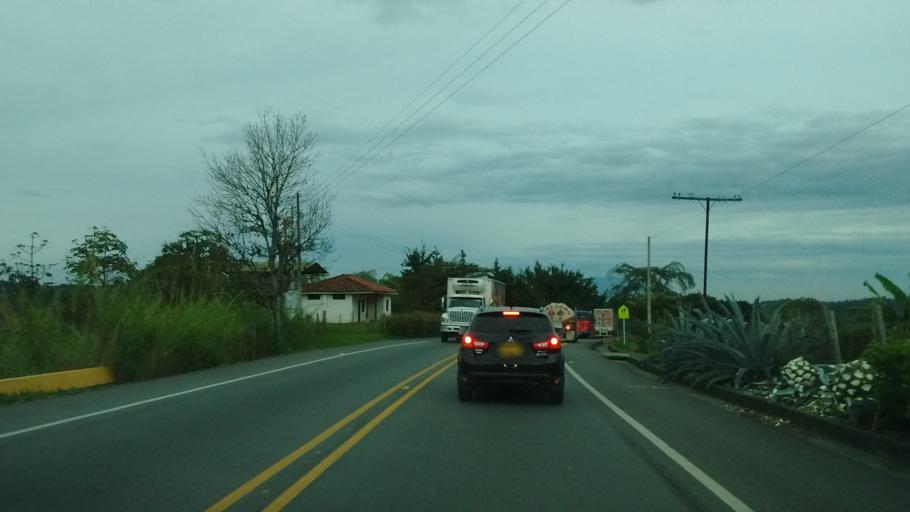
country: CO
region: Cauca
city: Morales
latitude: 2.7804
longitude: -76.5553
